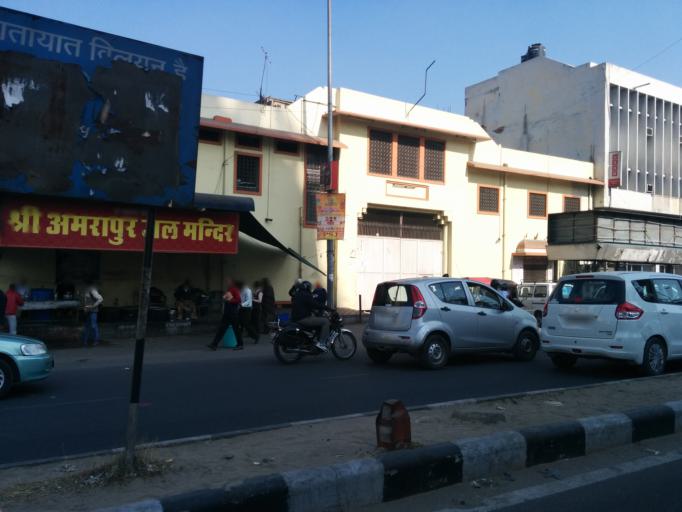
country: IN
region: Rajasthan
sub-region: Jaipur
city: Jaipur
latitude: 26.9183
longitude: 75.7999
